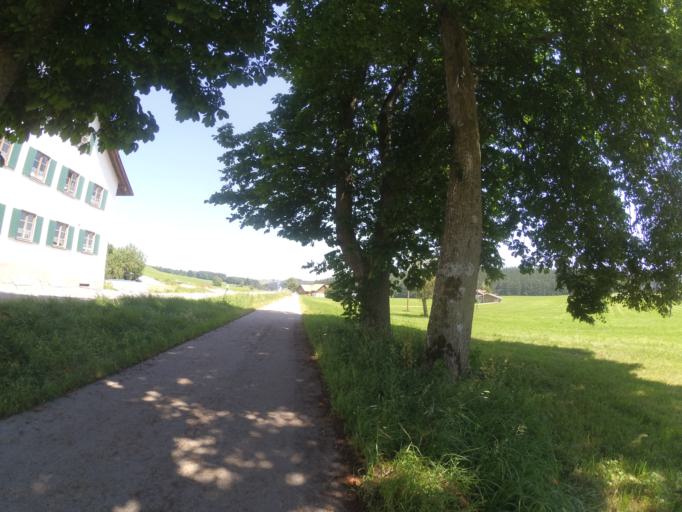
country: DE
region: Bavaria
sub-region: Swabia
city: Haldenwang
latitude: 47.8238
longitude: 10.3464
